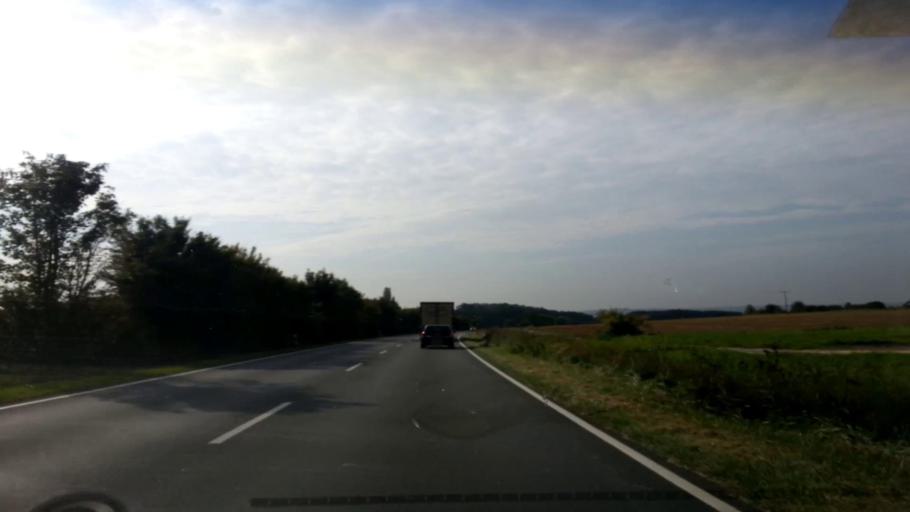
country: DE
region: Bavaria
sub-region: Regierungsbezirk Unterfranken
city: Prichsenstadt
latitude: 49.8086
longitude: 10.3611
